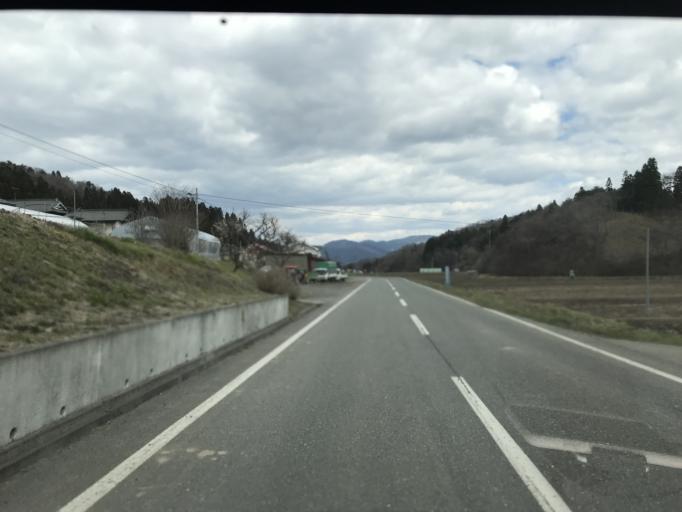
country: JP
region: Iwate
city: Ichinoseki
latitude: 38.9608
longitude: 141.0883
